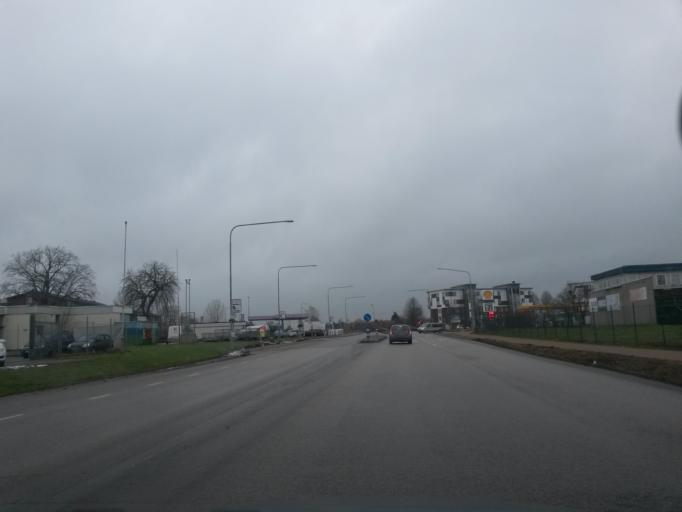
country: SE
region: Vaestra Goetaland
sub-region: Vanersborgs Kommun
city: Vanersborg
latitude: 58.3657
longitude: 12.3243
